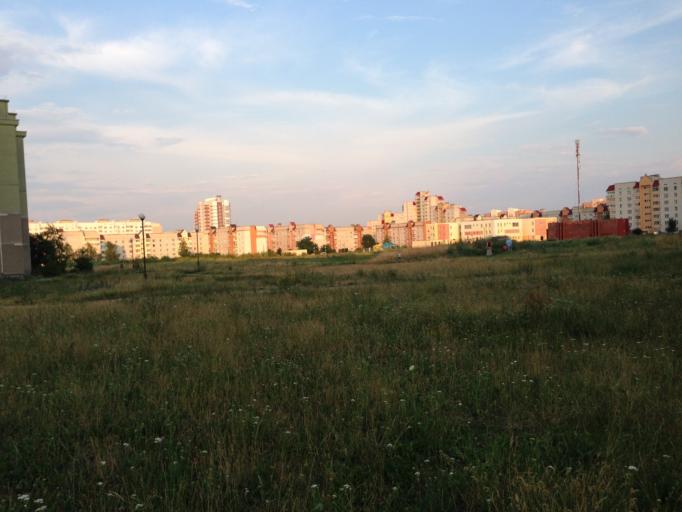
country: BY
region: Grodnenskaya
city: Hrodna
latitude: 53.7143
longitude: 23.8522
